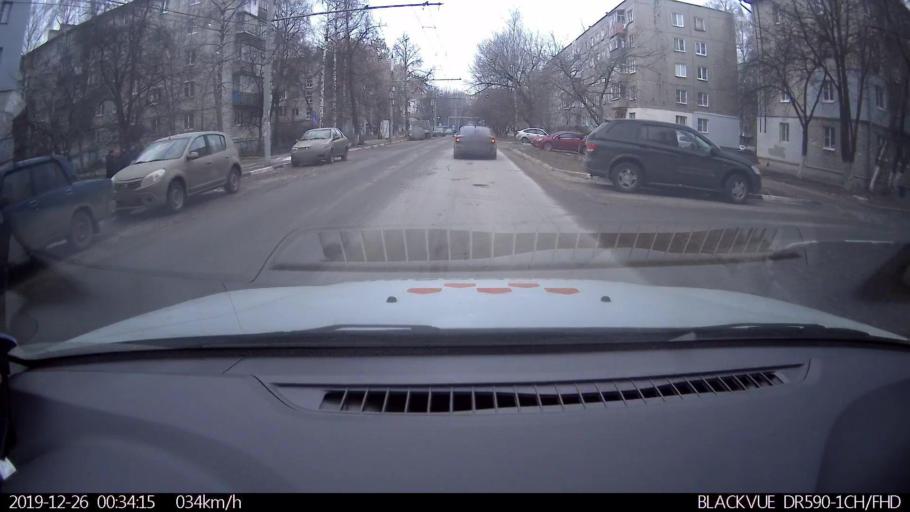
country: RU
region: Nizjnij Novgorod
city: Nizhniy Novgorod
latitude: 56.2893
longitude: 43.9176
